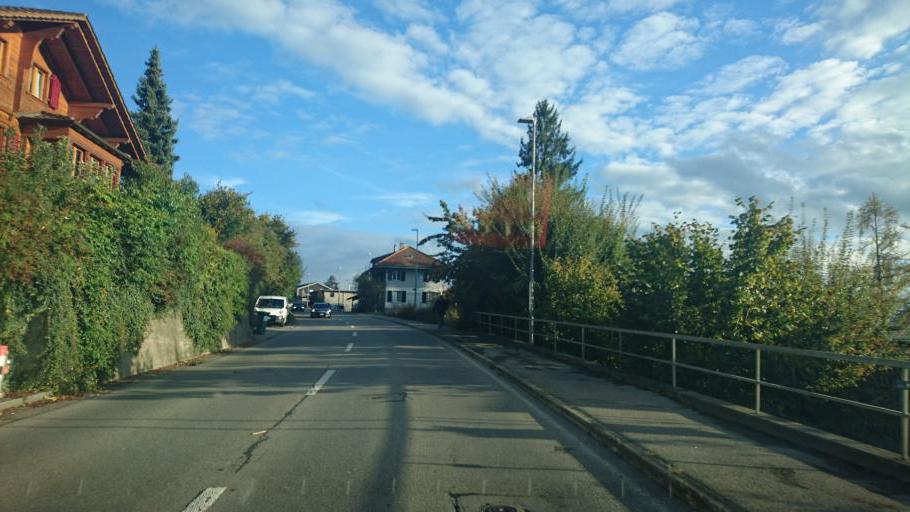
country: CH
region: Bern
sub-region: Bern-Mittelland District
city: Worb
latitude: 46.9291
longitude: 7.5672
